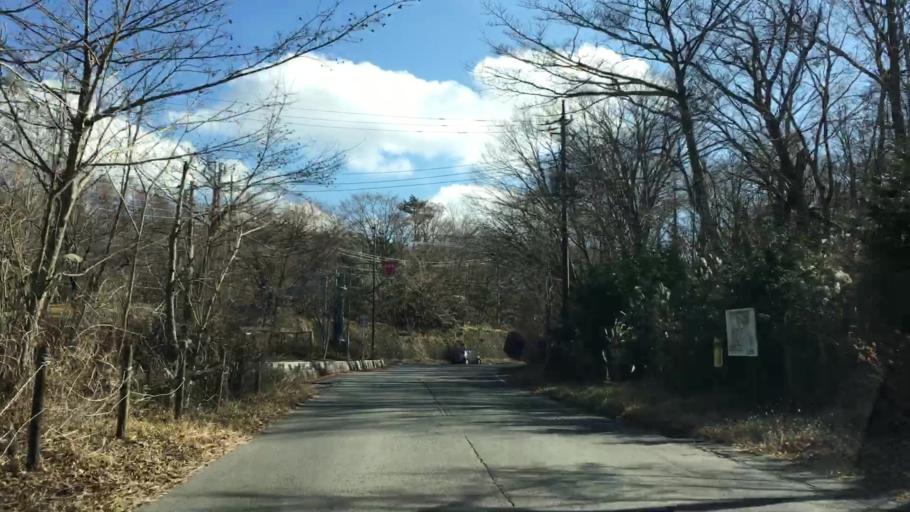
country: JP
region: Shizuoka
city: Gotemba
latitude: 35.3943
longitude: 138.8633
